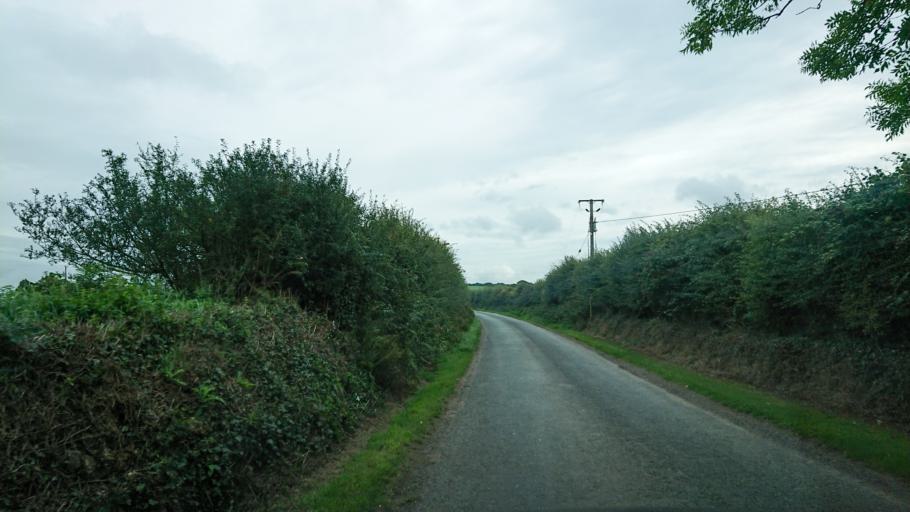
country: IE
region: Munster
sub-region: Waterford
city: Dunmore East
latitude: 52.1794
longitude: -6.9950
